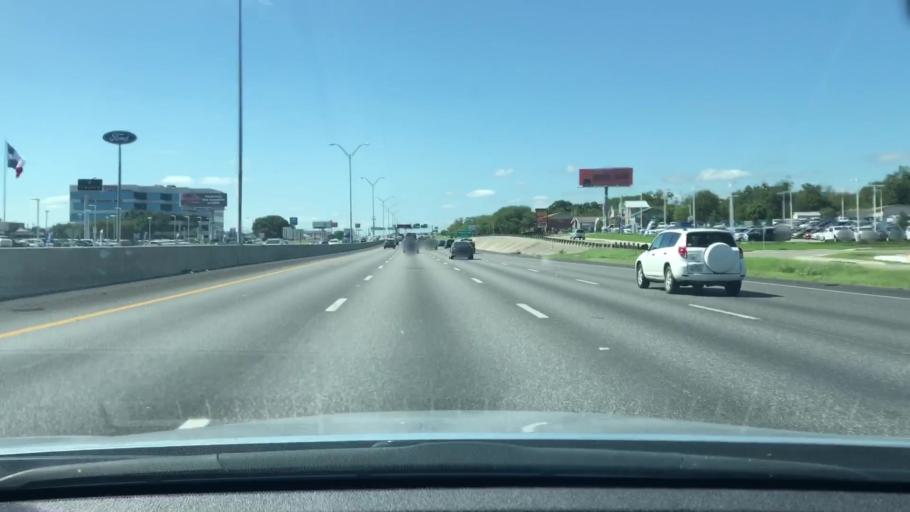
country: US
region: Texas
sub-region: Comal County
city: New Braunfels
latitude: 29.6902
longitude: -98.1148
